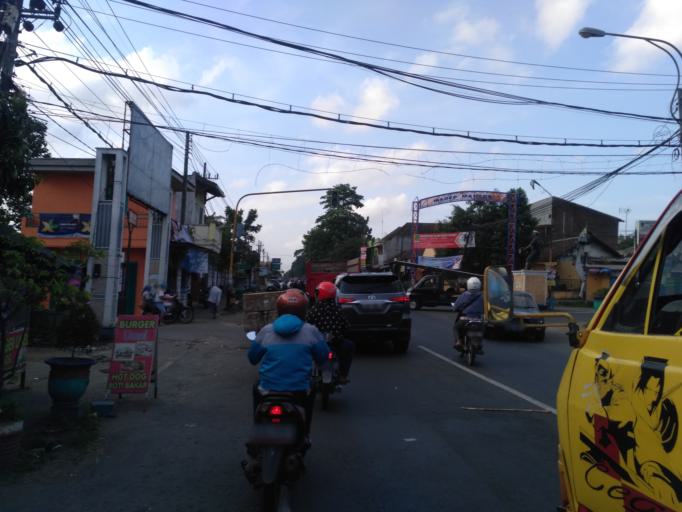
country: ID
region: East Java
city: Pakisaji
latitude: -8.0636
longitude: 112.5999
